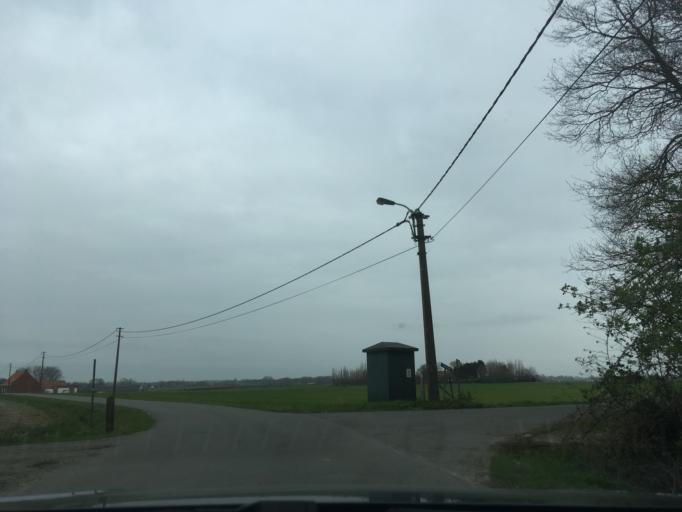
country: BE
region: Flanders
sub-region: Provincie West-Vlaanderen
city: Lichtervelde
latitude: 51.0016
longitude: 3.1510
